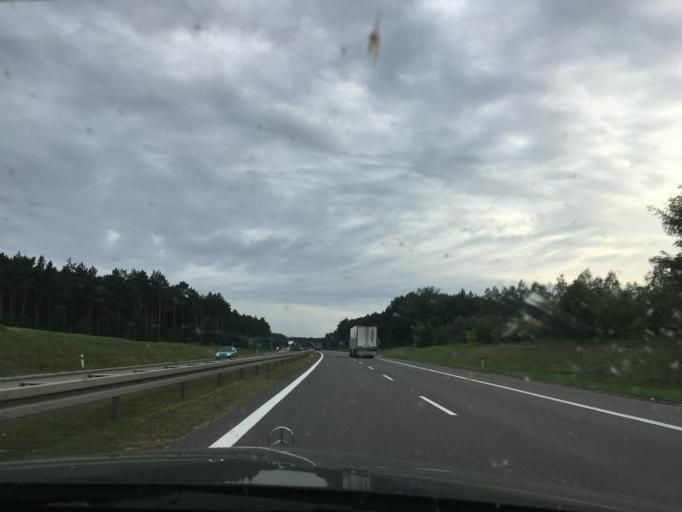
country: PL
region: Masovian Voivodeship
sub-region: Powiat ostrowski
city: Ostrow Mazowiecka
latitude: 52.7985
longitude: 21.8691
